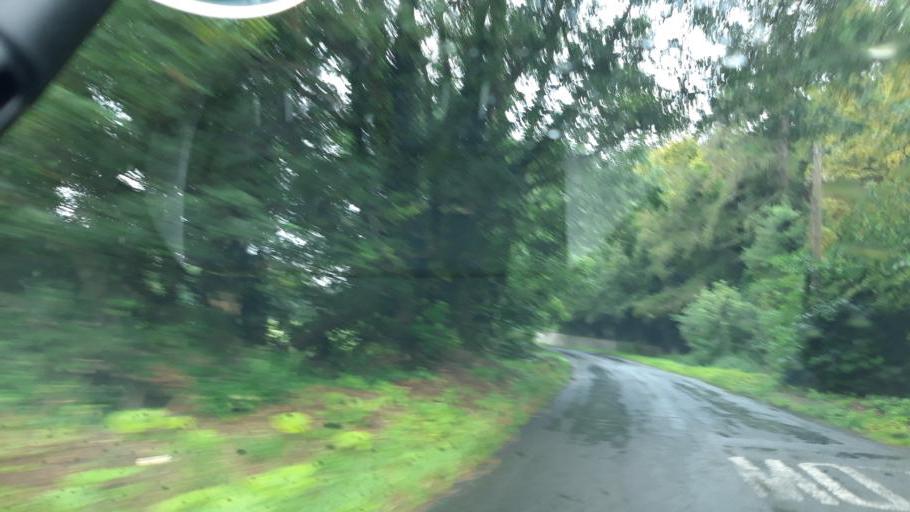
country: IE
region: Leinster
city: Hartstown
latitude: 53.3679
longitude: -6.4181
